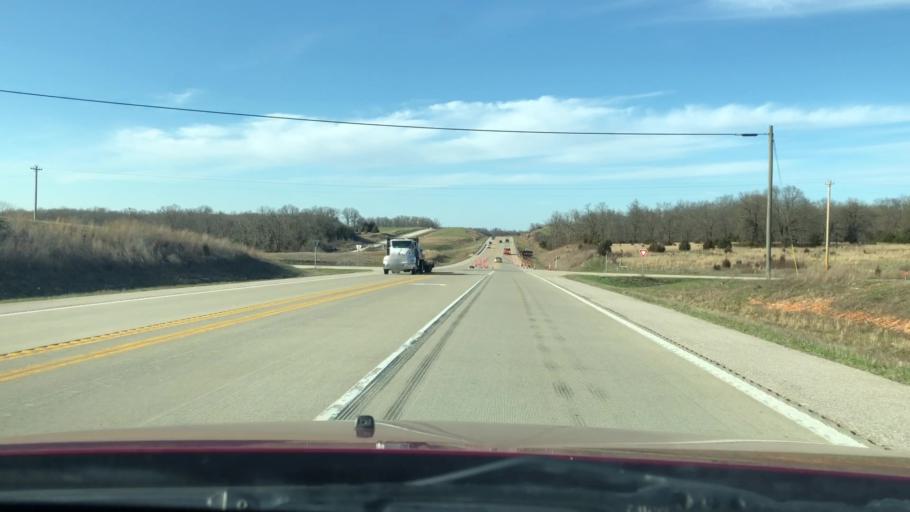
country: US
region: Missouri
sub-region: Camden County
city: Camdenton
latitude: 37.9513
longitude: -92.7154
